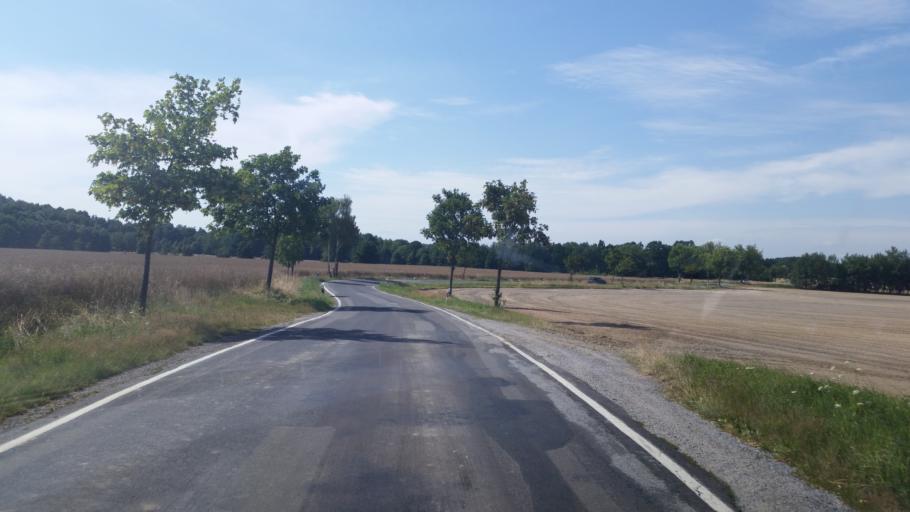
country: DE
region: Saxony
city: Neukirch
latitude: 51.3202
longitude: 14.0241
